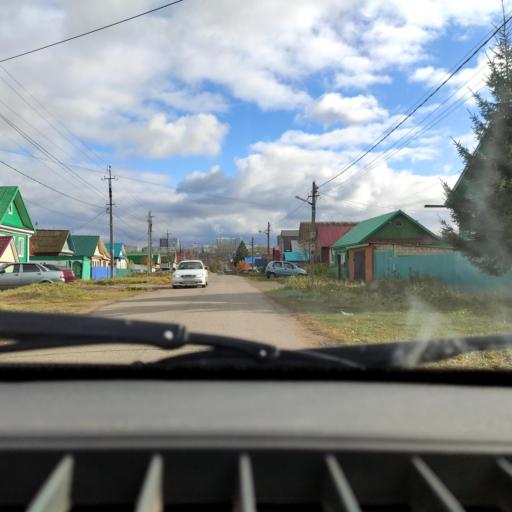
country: RU
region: Bashkortostan
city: Ufa
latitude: 54.7425
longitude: 55.9050
